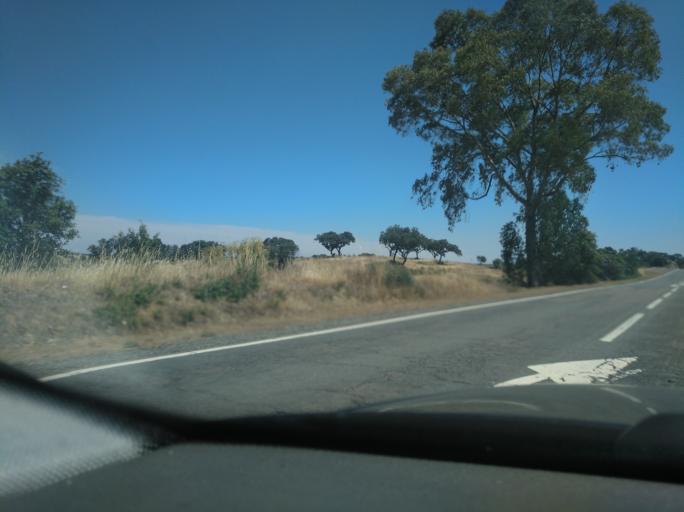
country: PT
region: Beja
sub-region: Castro Verde
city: Castro Verde
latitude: 37.6518
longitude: -8.0813
